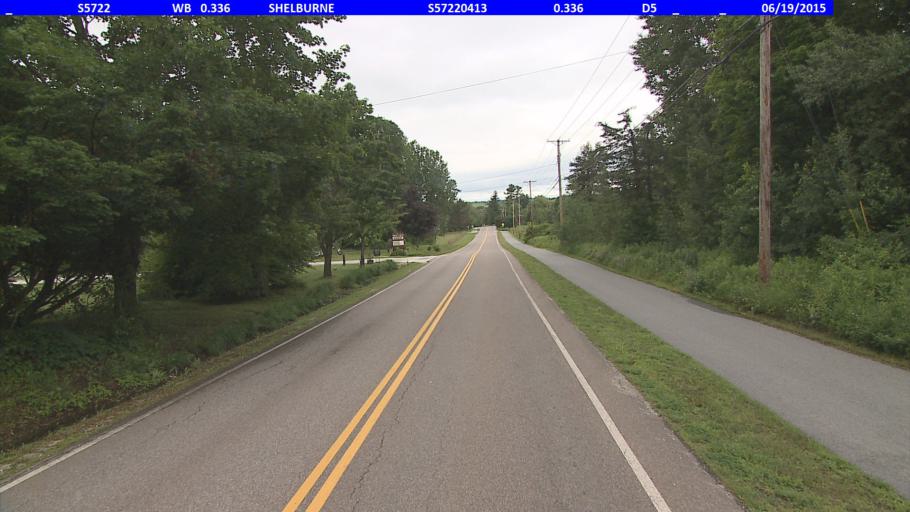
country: US
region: Vermont
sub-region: Chittenden County
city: Burlington
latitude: 44.3886
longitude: -73.2184
